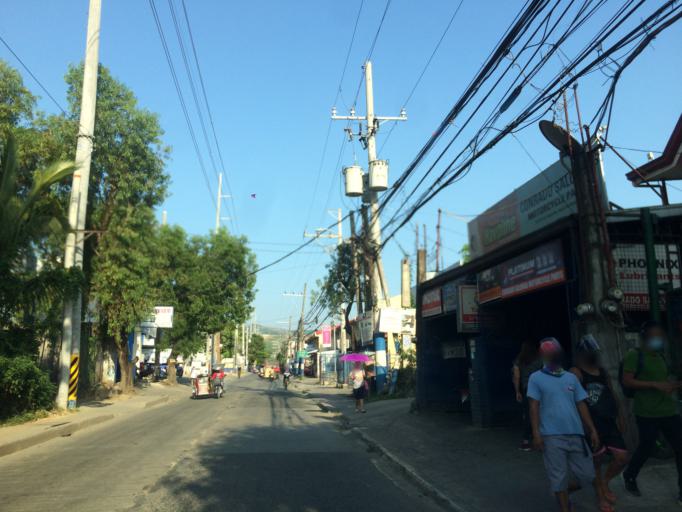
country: PH
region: Calabarzon
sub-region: Province of Rizal
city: San Mateo
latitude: 14.6812
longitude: 121.1184
